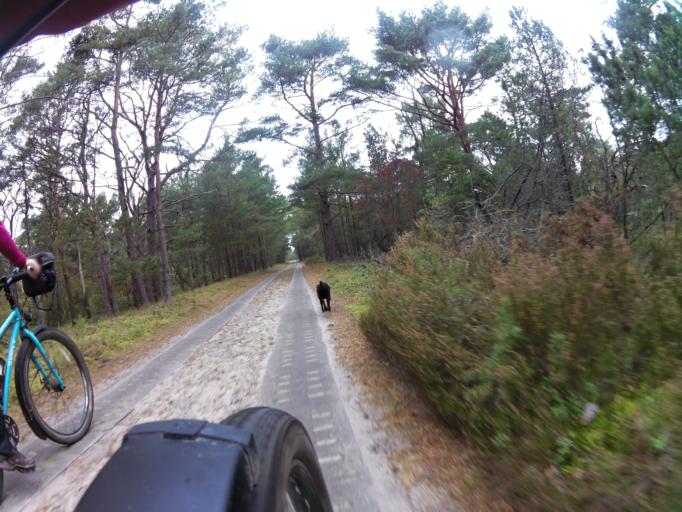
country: PL
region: Pomeranian Voivodeship
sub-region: Powiat pucki
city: Hel
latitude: 54.6259
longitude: 18.8156
